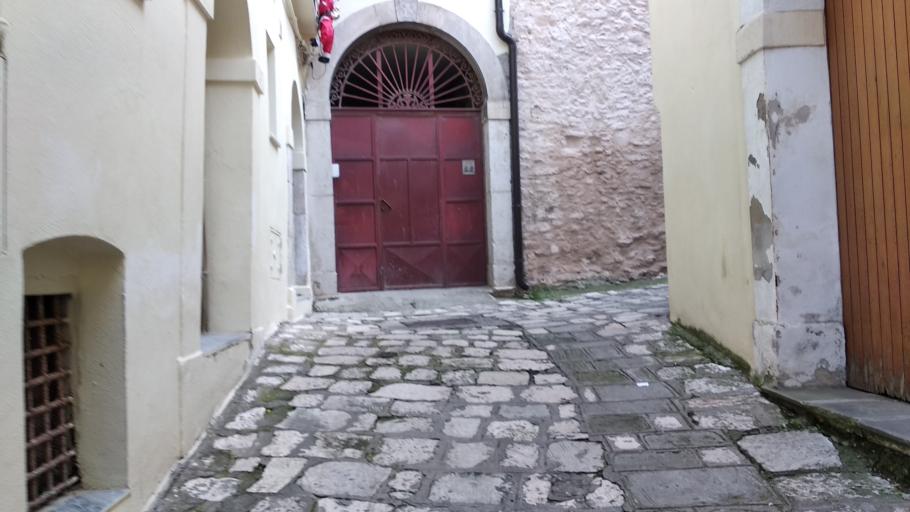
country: IT
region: Basilicate
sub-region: Provincia di Matera
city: Tricarico
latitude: 40.6240
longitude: 16.1431
